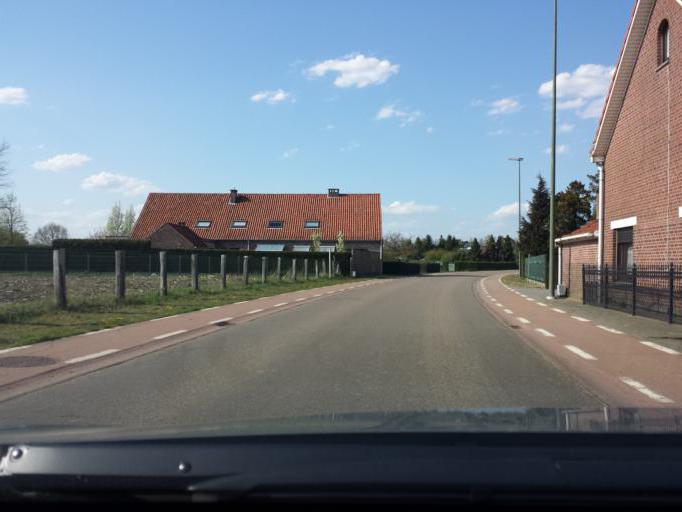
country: BE
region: Flanders
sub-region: Provincie Limburg
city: Halen
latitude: 50.9619
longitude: 5.1155
